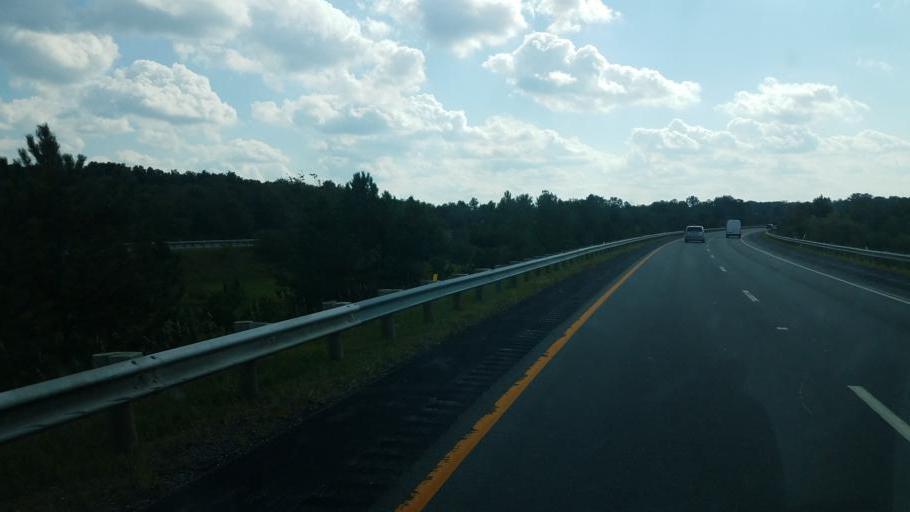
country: US
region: Ohio
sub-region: Medina County
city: Medina
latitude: 41.1653
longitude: -81.7678
